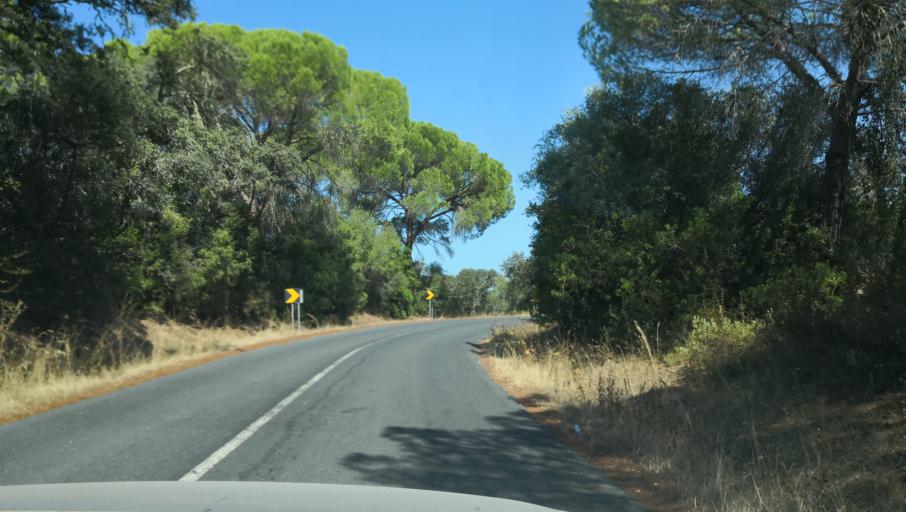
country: PT
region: Setubal
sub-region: Alcacer do Sal
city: Alcacer do Sal
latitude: 38.2896
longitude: -8.4044
